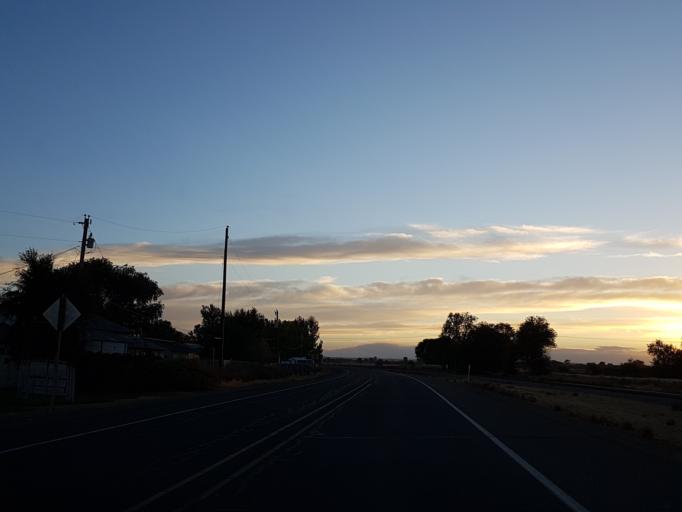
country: US
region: Oregon
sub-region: Malheur County
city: Vale
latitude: 43.9813
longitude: -117.2529
